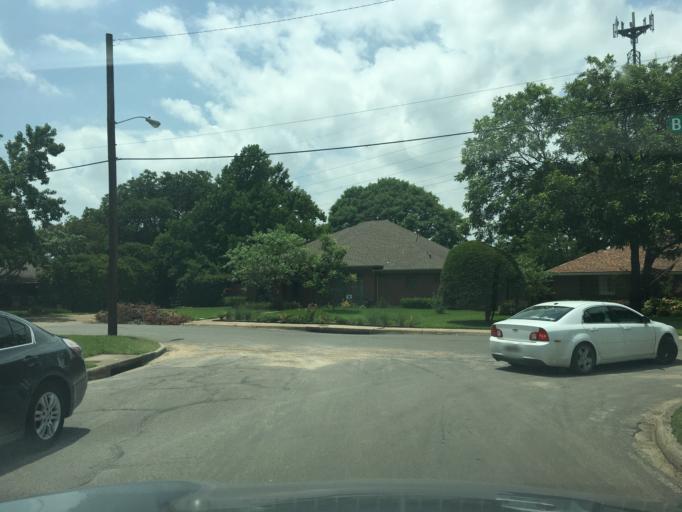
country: US
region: Texas
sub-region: Dallas County
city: Addison
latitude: 32.9012
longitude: -96.8338
